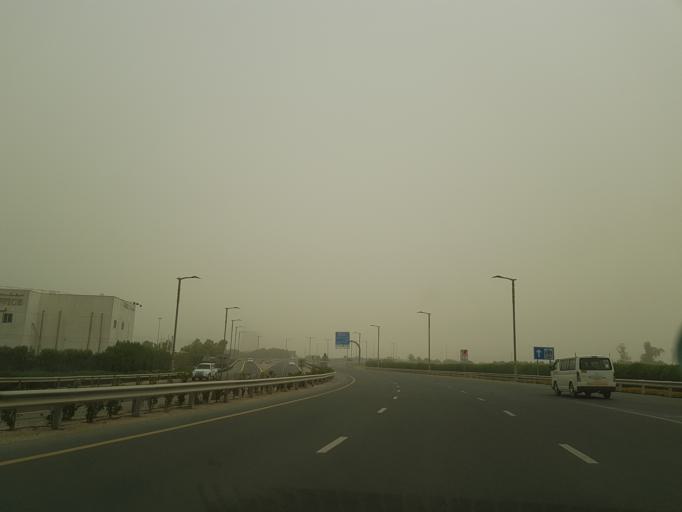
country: AE
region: Dubai
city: Dubai
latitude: 25.1713
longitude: 55.3177
